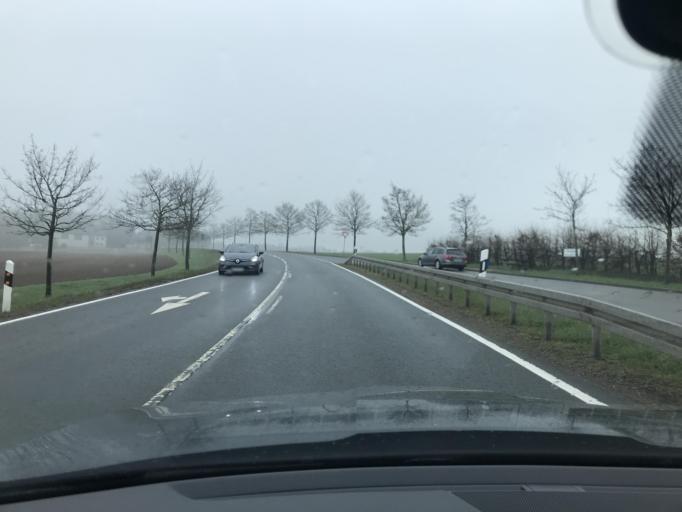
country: DE
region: Saxony-Anhalt
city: Harzgerode
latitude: 51.6300
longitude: 11.1456
